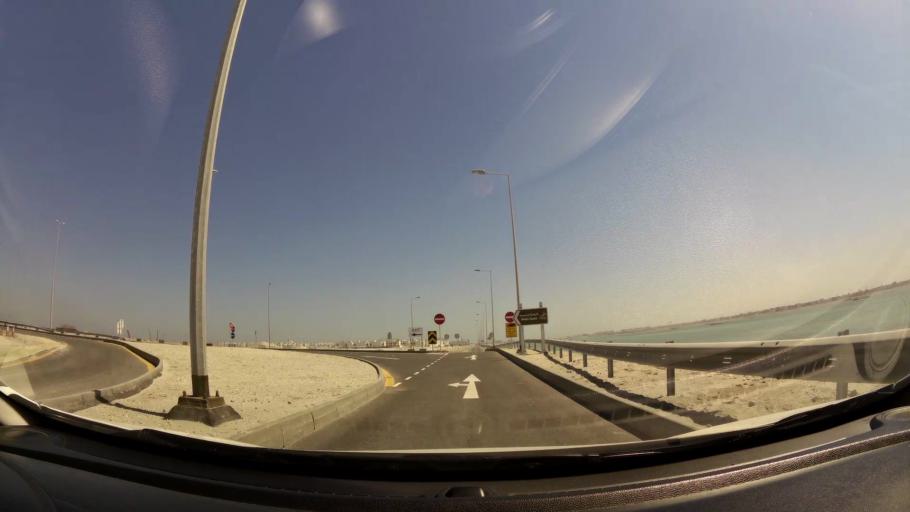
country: BH
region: Muharraq
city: Al Muharraq
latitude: 26.3036
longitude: 50.6263
